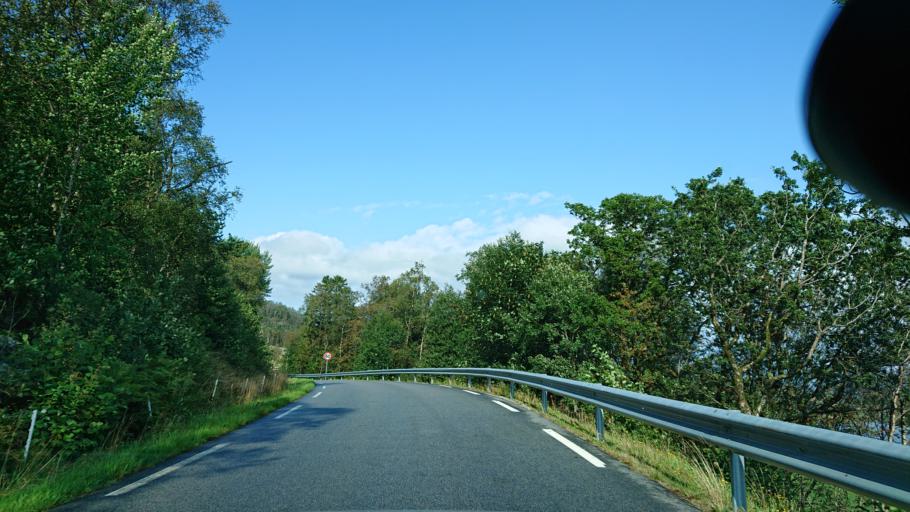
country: NO
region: Rogaland
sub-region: Gjesdal
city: Algard
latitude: 58.6917
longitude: 5.8802
